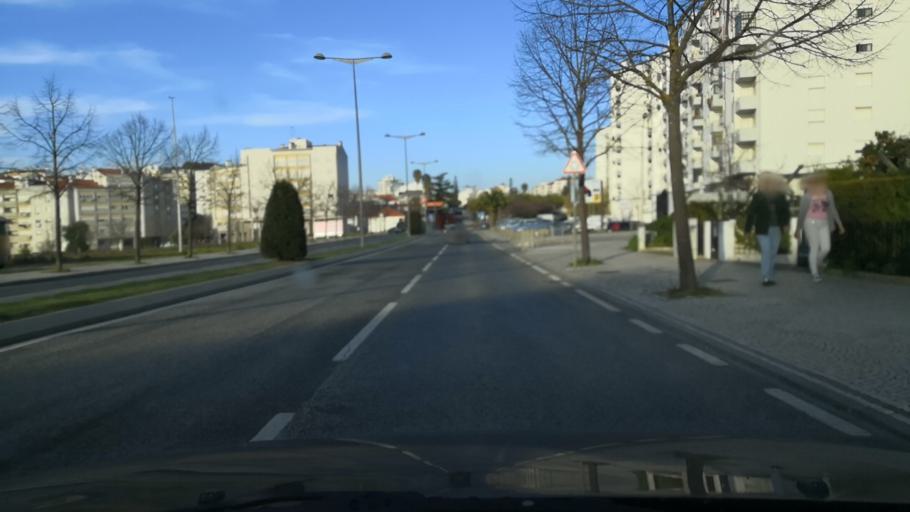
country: PT
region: Castelo Branco
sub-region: Castelo Branco
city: Castelo Branco
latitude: 39.8150
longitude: -7.5032
